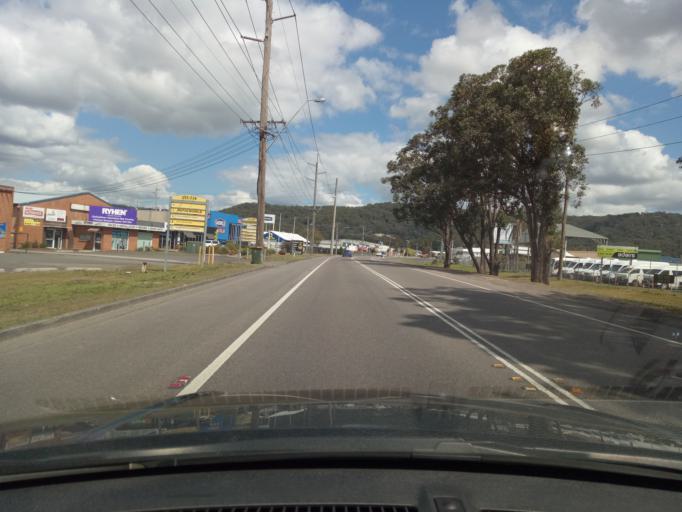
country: AU
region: New South Wales
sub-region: Gosford Shire
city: Gosford
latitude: -33.4163
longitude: 151.3284
